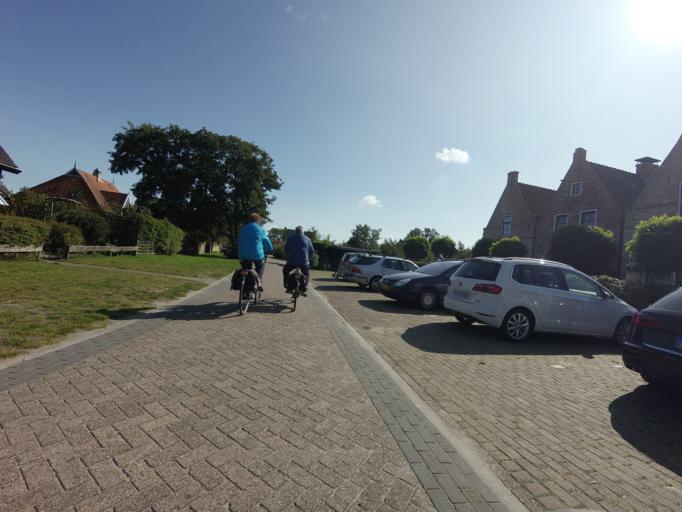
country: NL
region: Friesland
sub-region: Gemeente Terschelling
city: West-Terschelling
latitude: 53.3967
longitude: 5.3365
